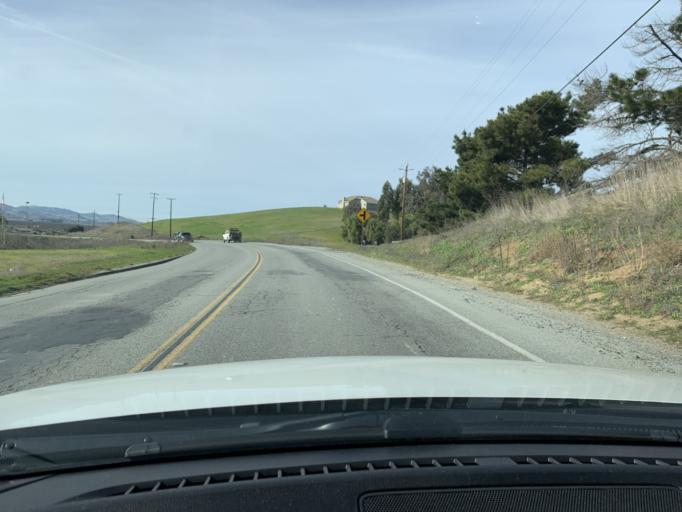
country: US
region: California
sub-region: San Benito County
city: Hollister
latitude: 36.8377
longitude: -121.4499
